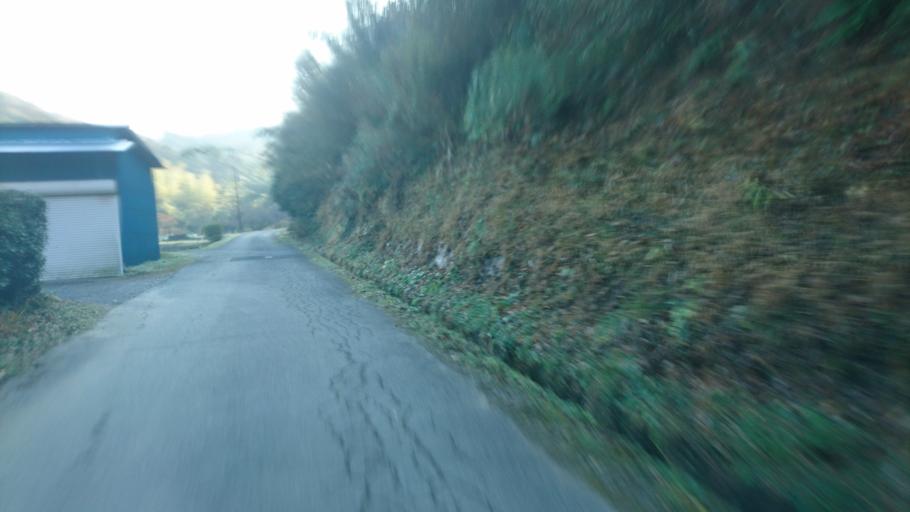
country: JP
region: Chiba
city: Kimitsu
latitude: 35.2902
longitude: 139.9524
